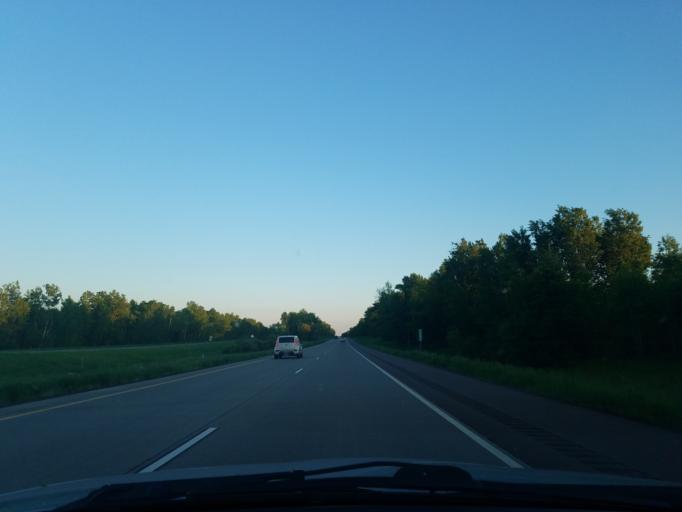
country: US
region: Minnesota
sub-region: Pine County
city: Sandstone
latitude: 46.2544
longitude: -92.8255
